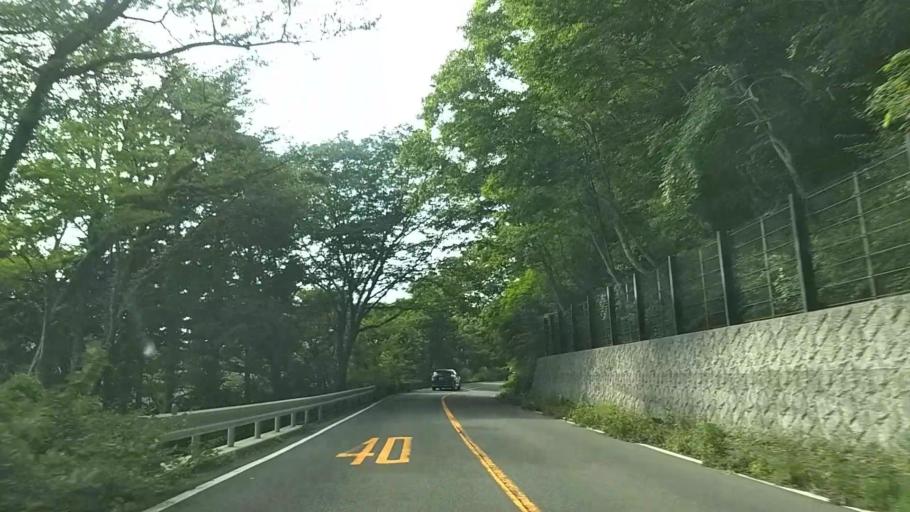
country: JP
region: Kanagawa
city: Hakone
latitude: 35.2277
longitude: 139.0010
